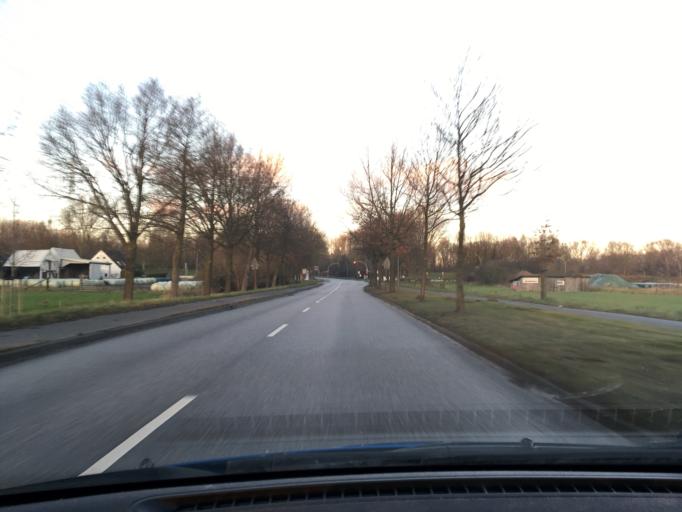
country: DE
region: Hamburg
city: Altona
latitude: 53.4938
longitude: 9.9092
